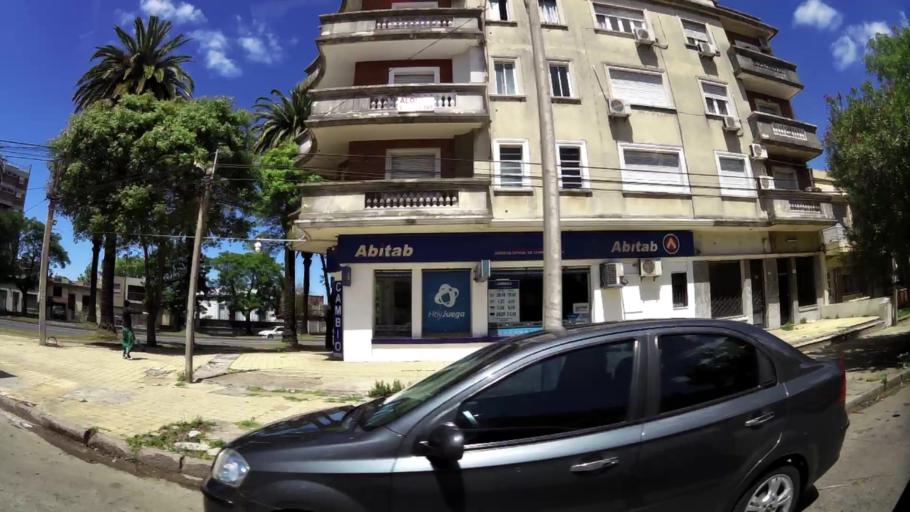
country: UY
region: Montevideo
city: Montevideo
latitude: -34.8704
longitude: -56.1793
